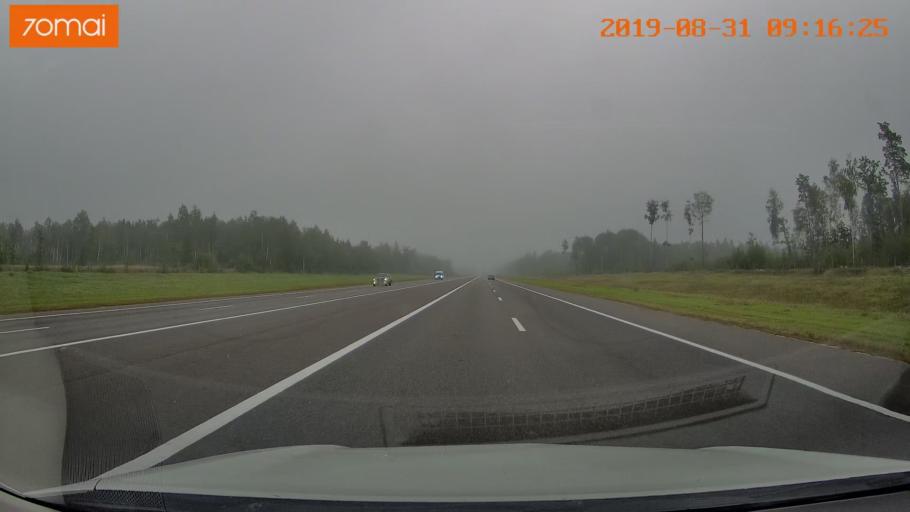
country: BY
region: Minsk
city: Chervyen'
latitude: 53.7709
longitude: 28.7098
